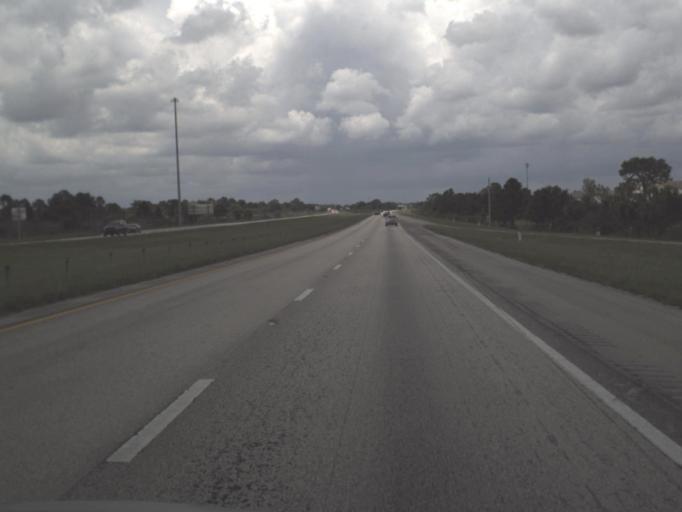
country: US
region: Florida
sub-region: Charlotte County
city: Harbour Heights
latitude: 26.9823
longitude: -82.0250
